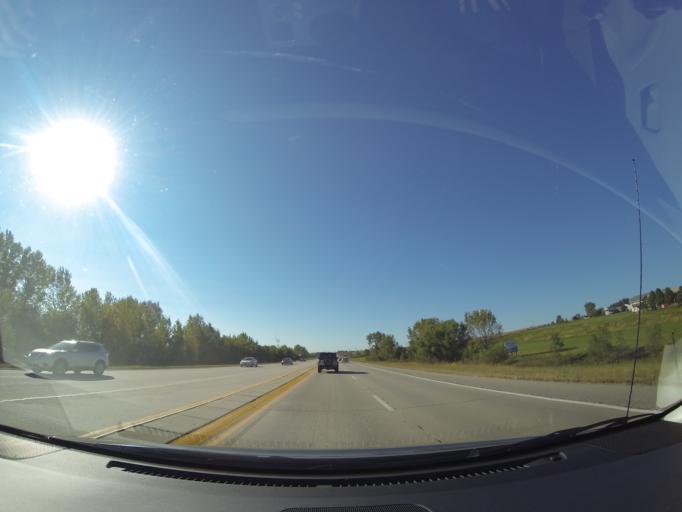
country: US
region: Nebraska
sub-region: Sarpy County
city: Gretna
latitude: 41.1210
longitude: -96.2532
